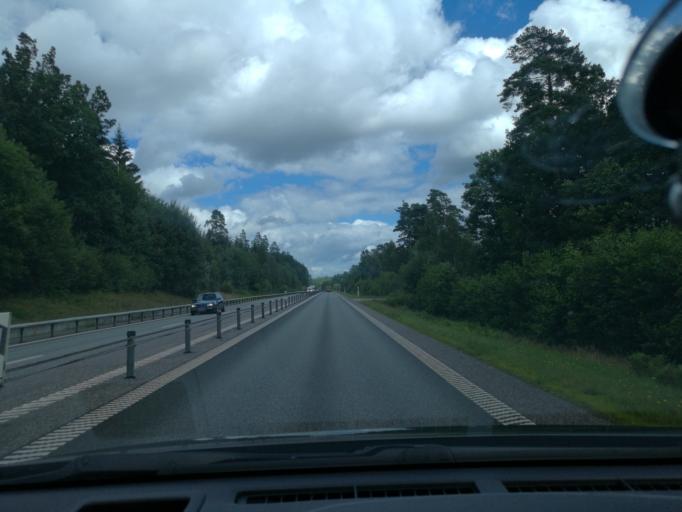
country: SE
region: Skane
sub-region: Hassleholms Kommun
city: Hastveda
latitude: 56.2312
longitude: 13.8921
